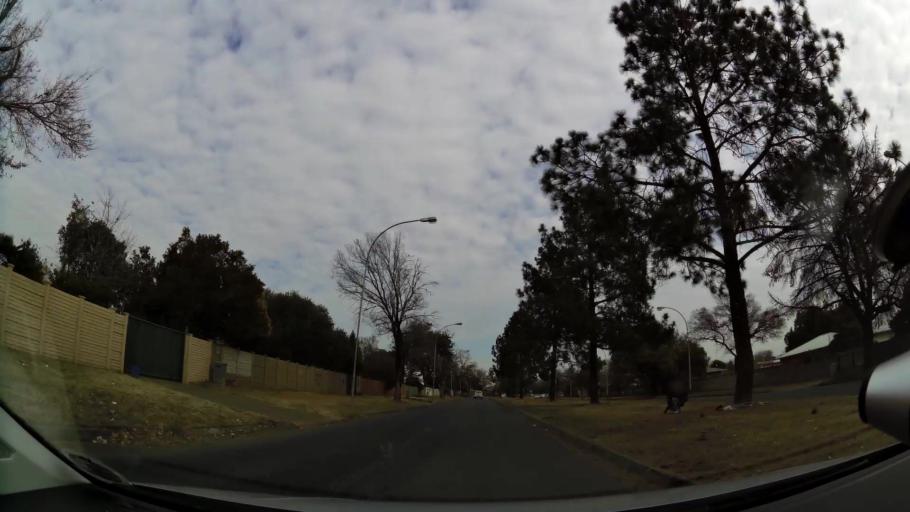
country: ZA
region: Orange Free State
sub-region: Mangaung Metropolitan Municipality
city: Bloemfontein
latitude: -29.1312
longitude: 26.1834
